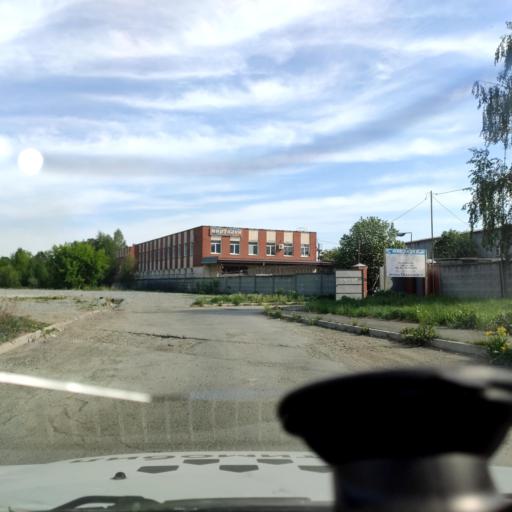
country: RU
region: Sverdlovsk
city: Sovkhoznyy
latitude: 56.7712
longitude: 60.5590
